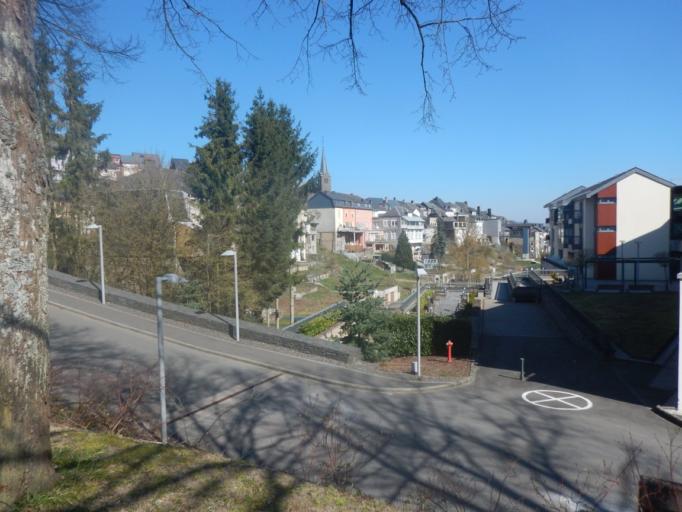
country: LU
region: Diekirch
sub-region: Canton de Wiltz
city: Wiltz
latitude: 49.9630
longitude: 5.9351
